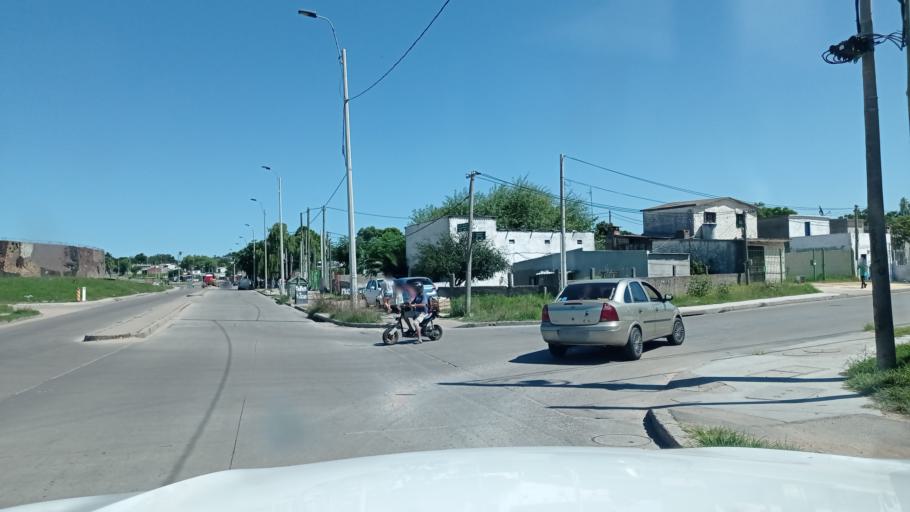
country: UY
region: Montevideo
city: Montevideo
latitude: -34.8663
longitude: -56.2531
